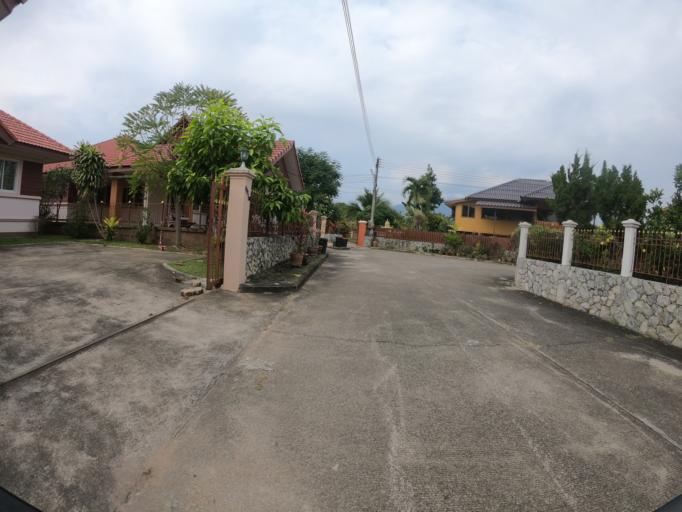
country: TH
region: Chiang Mai
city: Hang Dong
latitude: 18.7411
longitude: 98.9329
